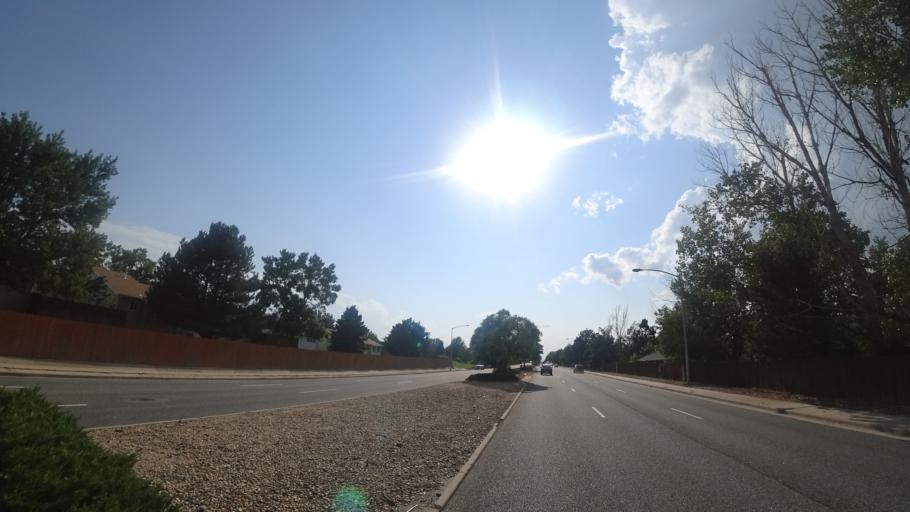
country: US
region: Colorado
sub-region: Arapahoe County
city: Dove Valley
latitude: 39.6386
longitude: -104.8019
